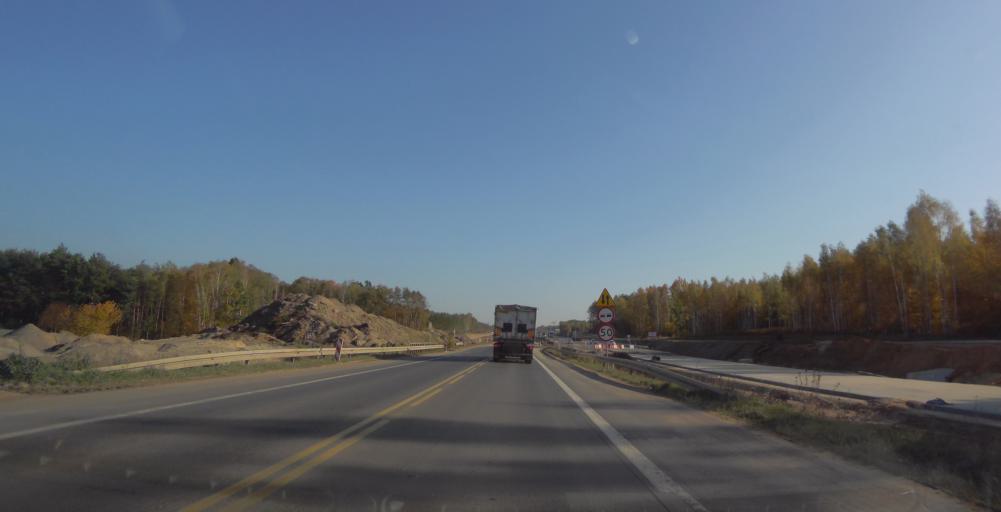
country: PL
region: Masovian Voivodeship
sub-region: Powiat otwocki
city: Celestynow
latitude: 52.1270
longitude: 21.3512
